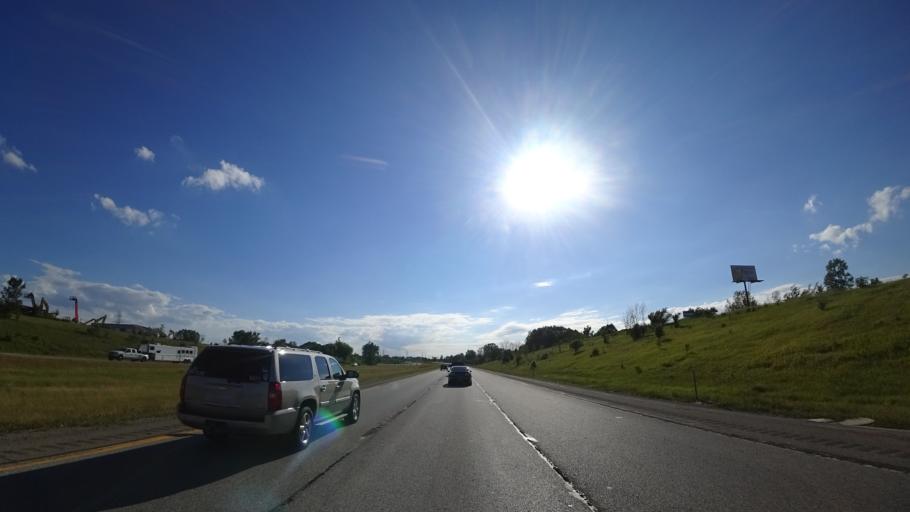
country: US
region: Michigan
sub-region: Ottawa County
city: Hudsonville
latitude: 42.8482
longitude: -85.8682
